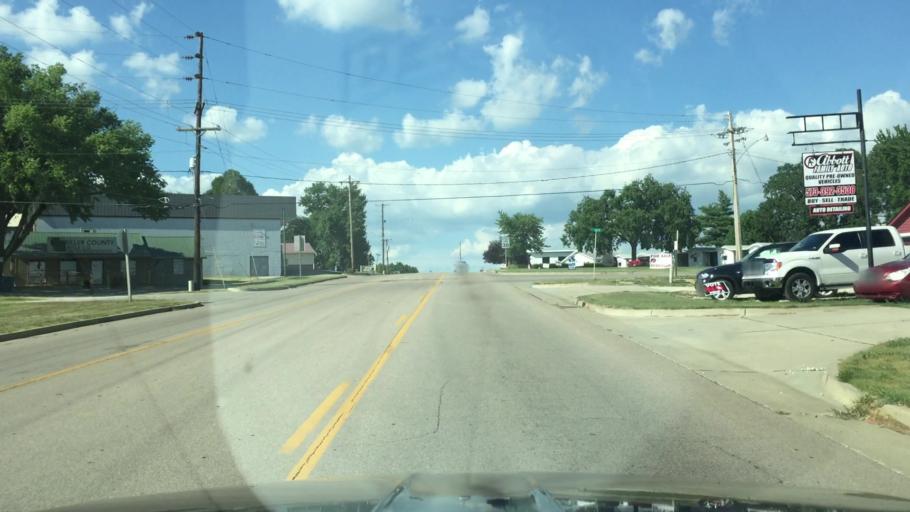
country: US
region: Missouri
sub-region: Miller County
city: Eldon
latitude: 38.3393
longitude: -92.5830
